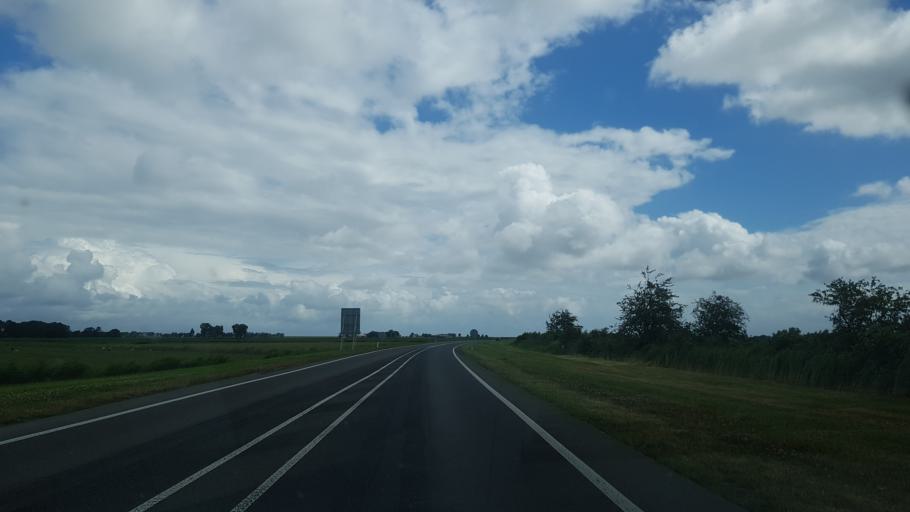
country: NL
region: Friesland
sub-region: Gemeente Dongeradeel
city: Anjum
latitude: 53.3713
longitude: 6.0930
